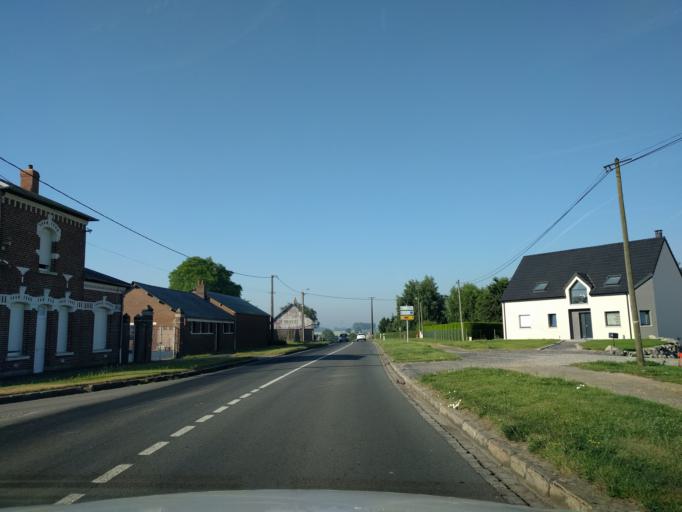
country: FR
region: Picardie
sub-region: Departement de la Somme
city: Peronne
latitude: 49.8731
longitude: 2.8938
